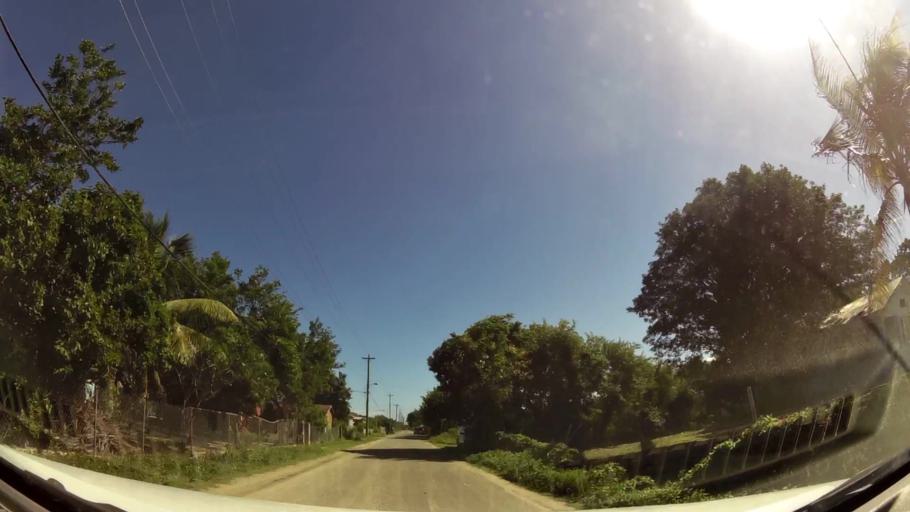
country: AG
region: Barbuda
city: Codrington
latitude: 17.6381
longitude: -61.8277
